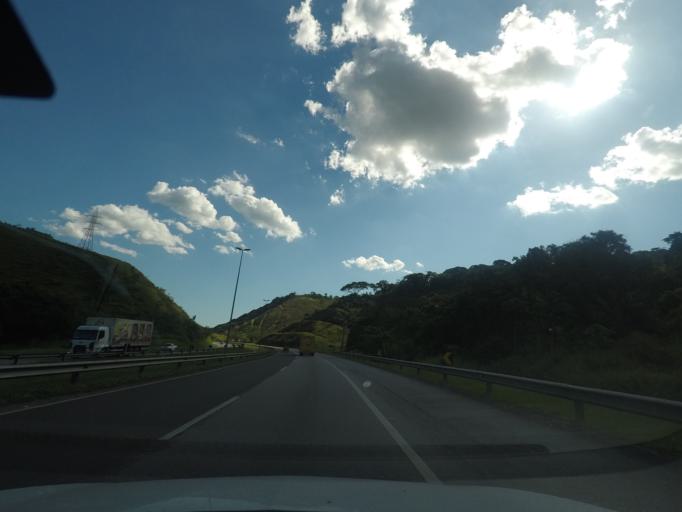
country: BR
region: Rio de Janeiro
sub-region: Guapimirim
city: Guapimirim
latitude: -22.5730
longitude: -43.0083
